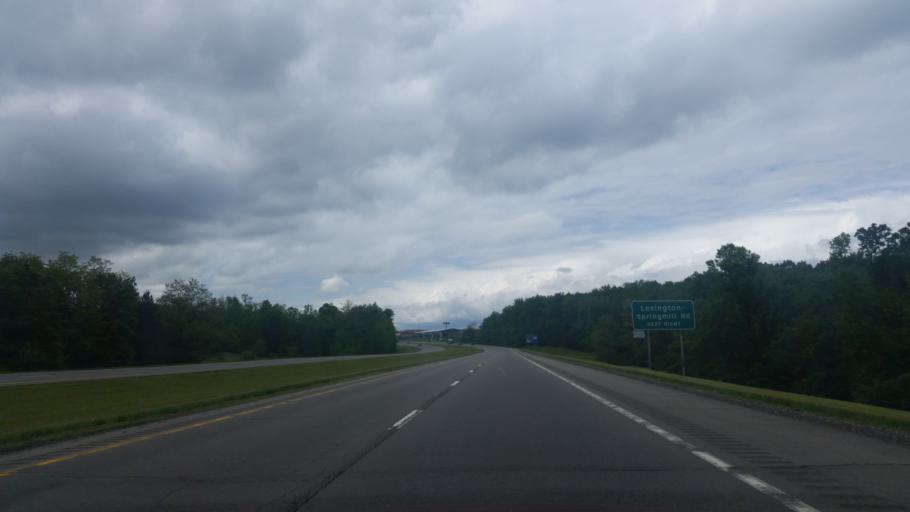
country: US
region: Ohio
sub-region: Richland County
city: Ontario
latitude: 40.7802
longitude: -82.5770
